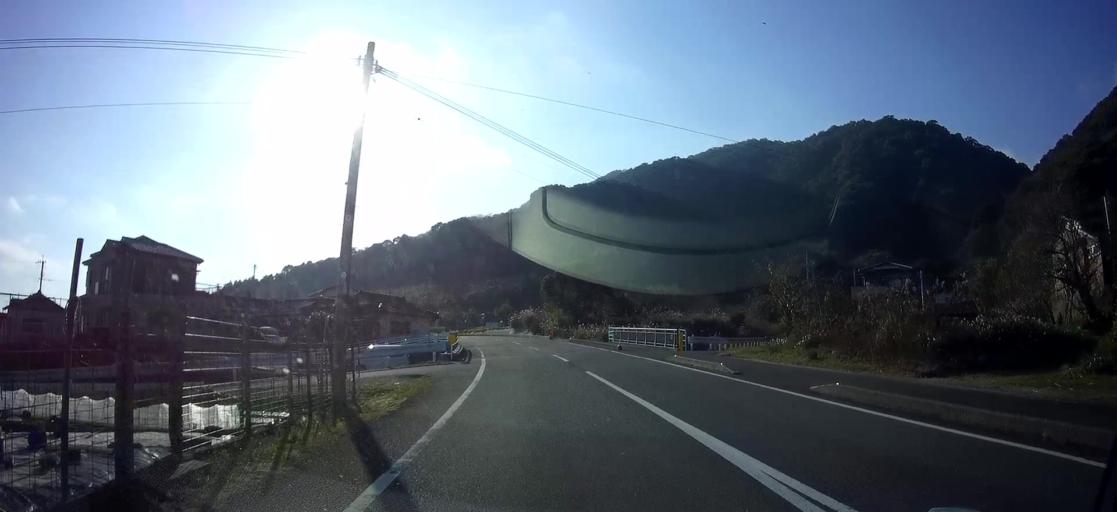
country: JP
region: Kumamoto
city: Minamata
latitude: 32.4032
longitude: 130.4008
